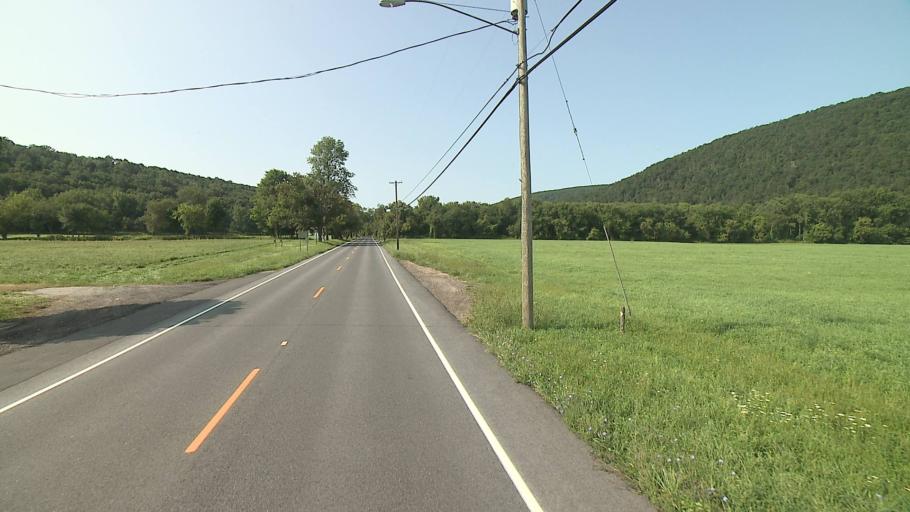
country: US
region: Connecticut
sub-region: Litchfield County
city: Kent
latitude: 41.7204
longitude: -73.4799
